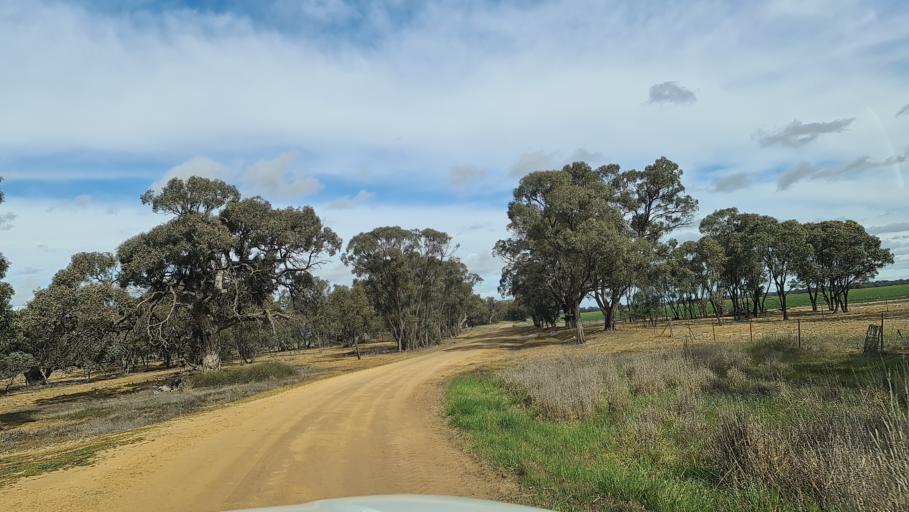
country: AU
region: Victoria
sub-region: Horsham
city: Horsham
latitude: -36.6356
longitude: 142.4118
